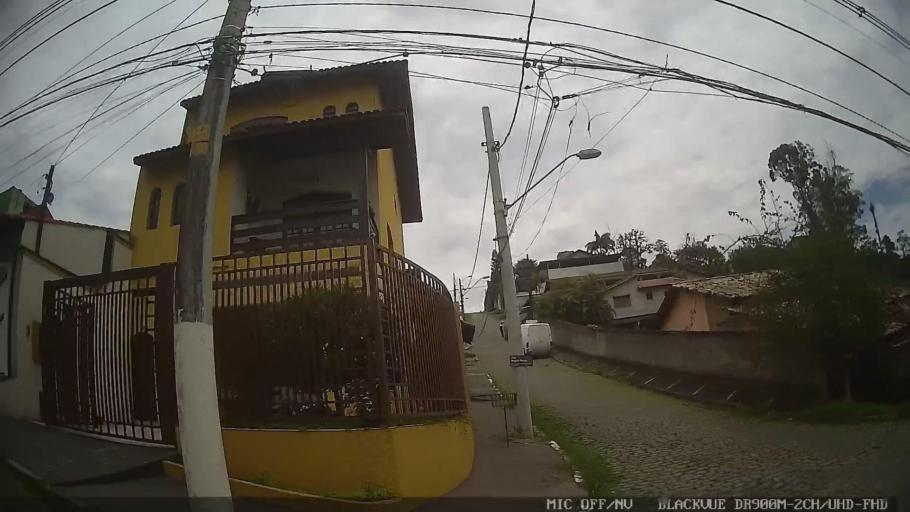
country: BR
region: Sao Paulo
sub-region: Ribeirao Pires
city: Ribeirao Pires
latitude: -23.7186
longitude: -46.4147
